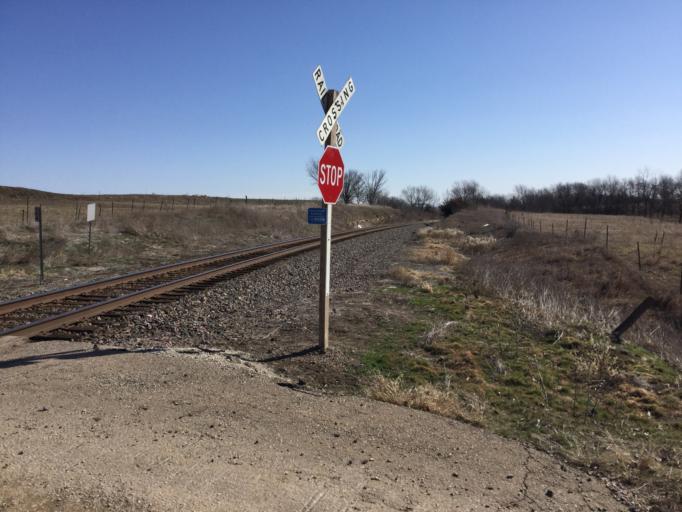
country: US
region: Kansas
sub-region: Marshall County
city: Marysville
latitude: 39.8603
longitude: -96.4637
